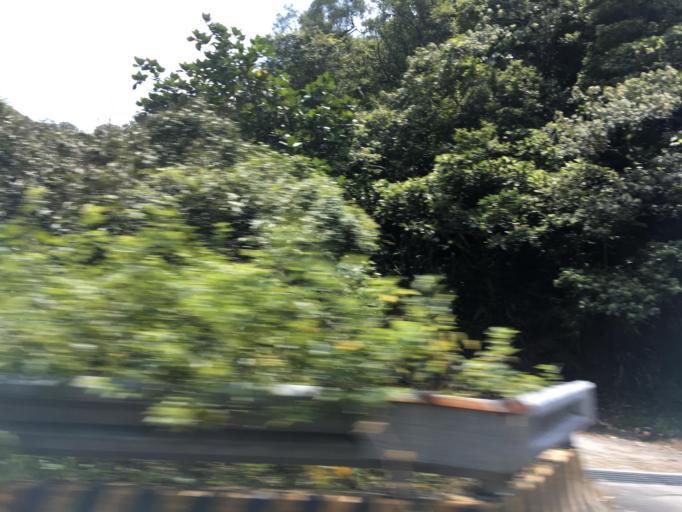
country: TW
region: Taiwan
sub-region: Yilan
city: Yilan
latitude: 24.8161
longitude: 121.7382
